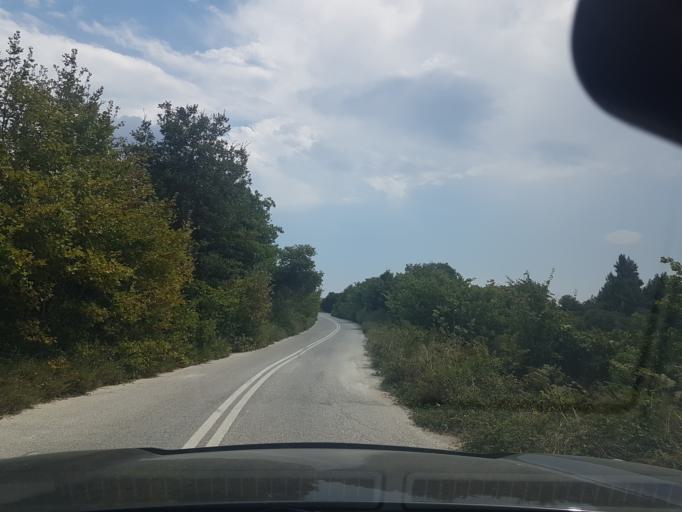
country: GR
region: Central Greece
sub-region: Nomos Evvoias
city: Kymi
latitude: 38.6450
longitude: 24.0508
